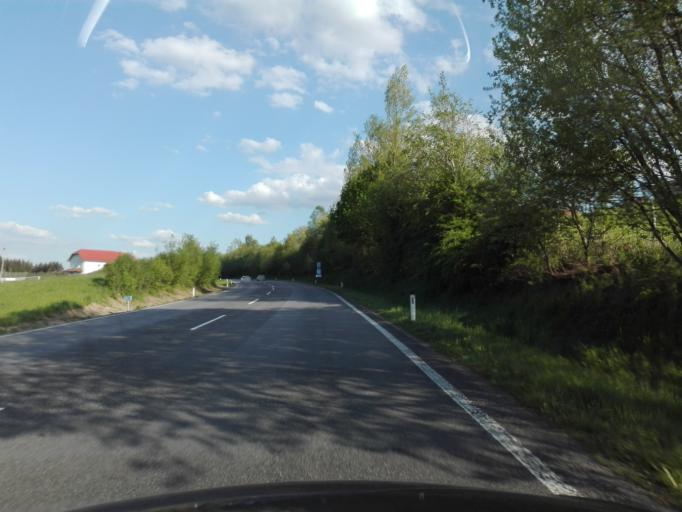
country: AT
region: Upper Austria
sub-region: Politischer Bezirk Rohrbach
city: Kleinzell im Muehlkreis
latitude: 48.4884
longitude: 13.9728
